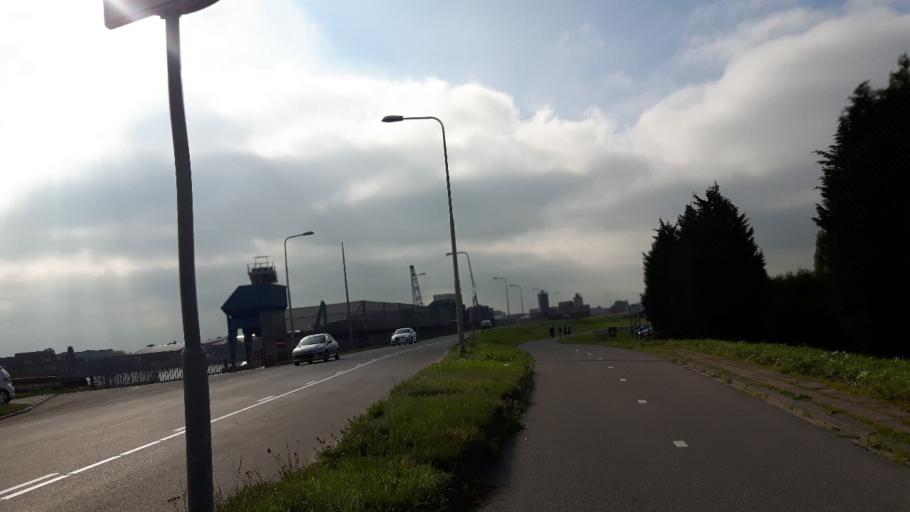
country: NL
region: South Holland
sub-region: Gemeente Gouda
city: Gouda
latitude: 51.9995
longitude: 4.6917
